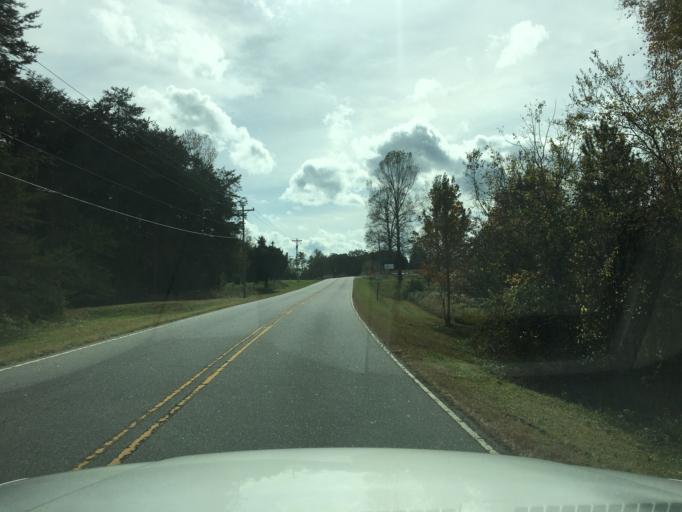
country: US
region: North Carolina
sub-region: Catawba County
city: Newton
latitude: 35.6644
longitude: -81.2721
